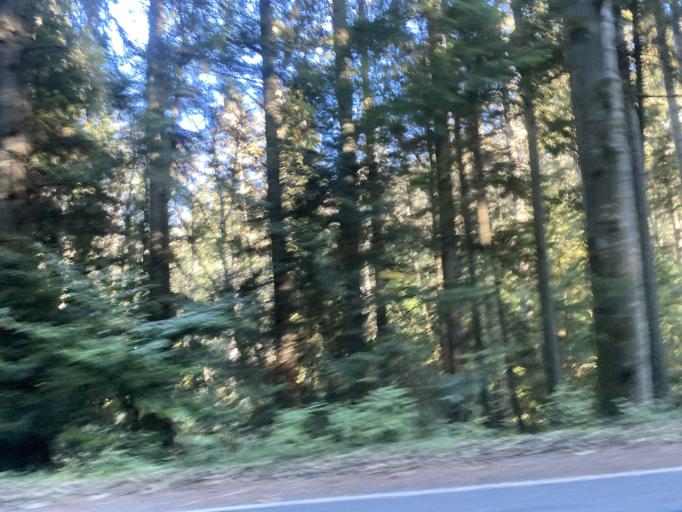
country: US
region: Washington
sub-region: Island County
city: Langley
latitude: 48.0324
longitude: -122.4228
